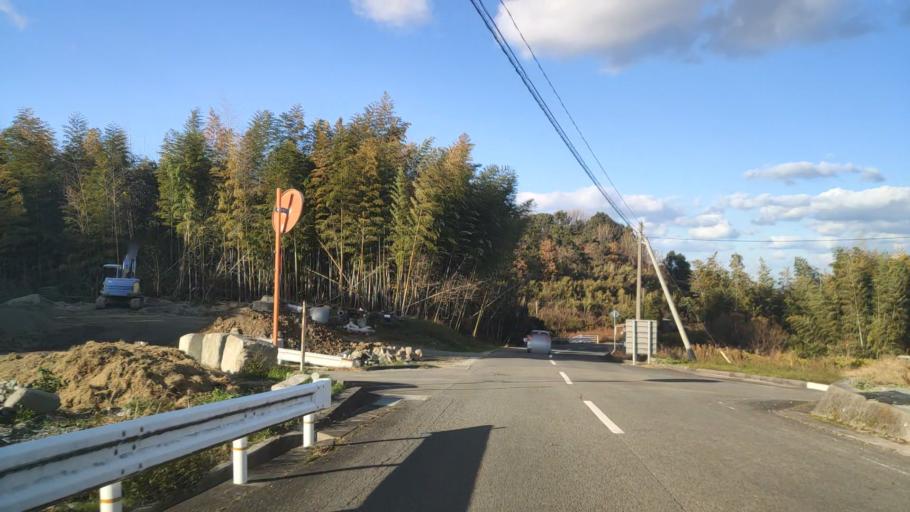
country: JP
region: Ehime
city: Saijo
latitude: 33.8871
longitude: 133.1291
